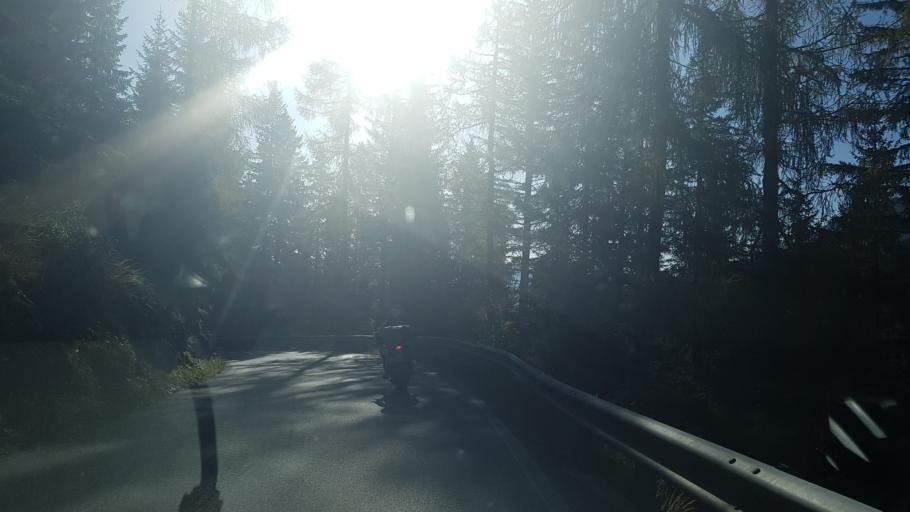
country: IT
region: Veneto
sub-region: Provincia di Belluno
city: Candide
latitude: 46.6504
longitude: 12.4464
